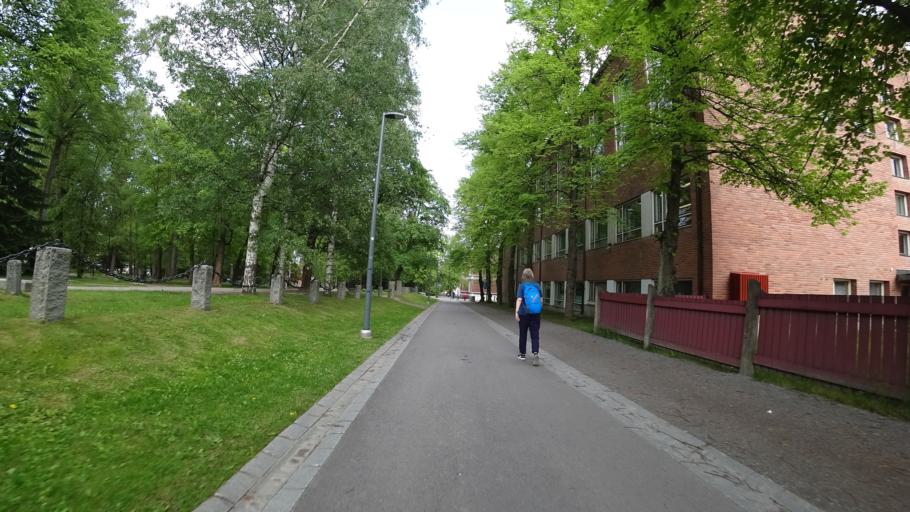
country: FI
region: Pirkanmaa
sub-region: Tampere
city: Tampere
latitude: 61.4966
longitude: 23.7457
